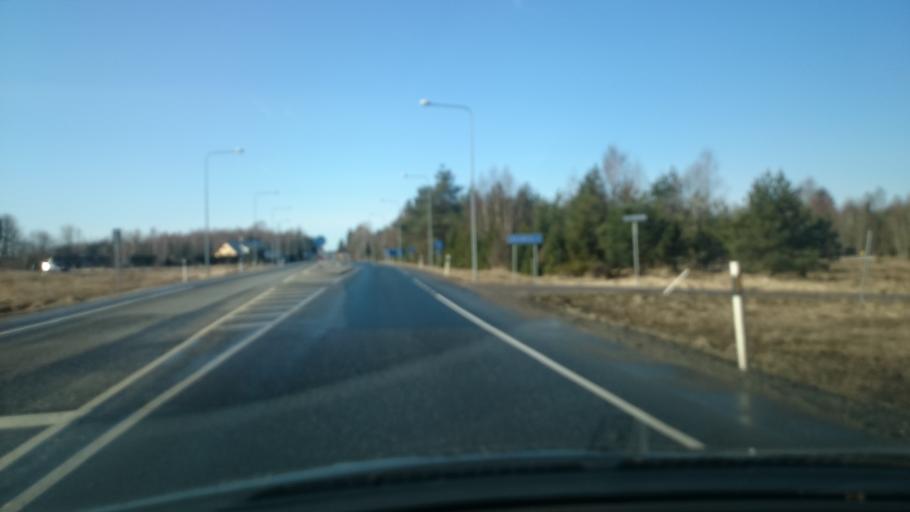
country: EE
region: Raplamaa
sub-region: Rapla vald
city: Rapla
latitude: 59.0408
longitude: 24.8381
